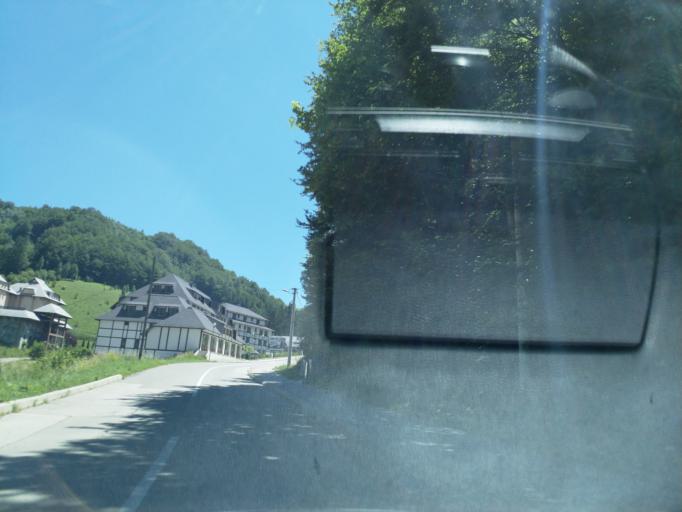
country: XK
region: Mitrovica
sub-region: Komuna e Leposaviqit
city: Leposaviq
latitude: 43.2920
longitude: 20.8799
